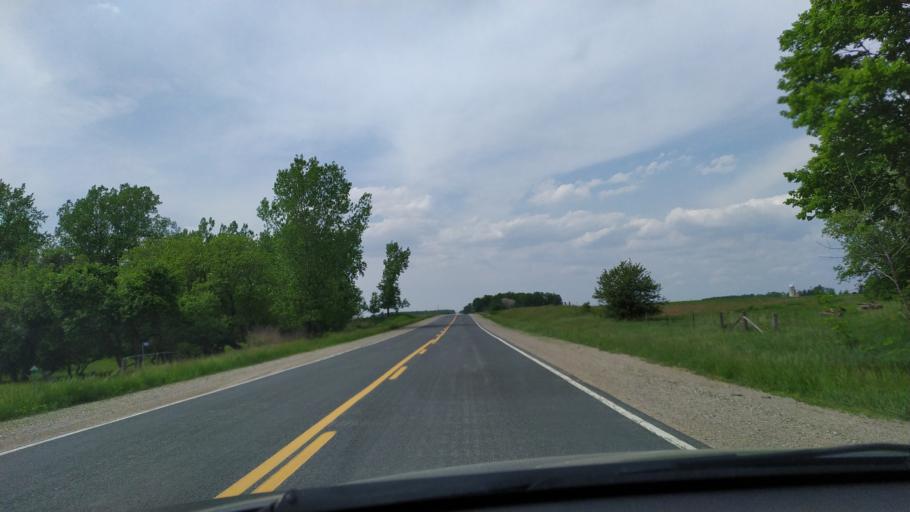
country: CA
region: Ontario
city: Ingersoll
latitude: 43.0221
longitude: -80.9688
